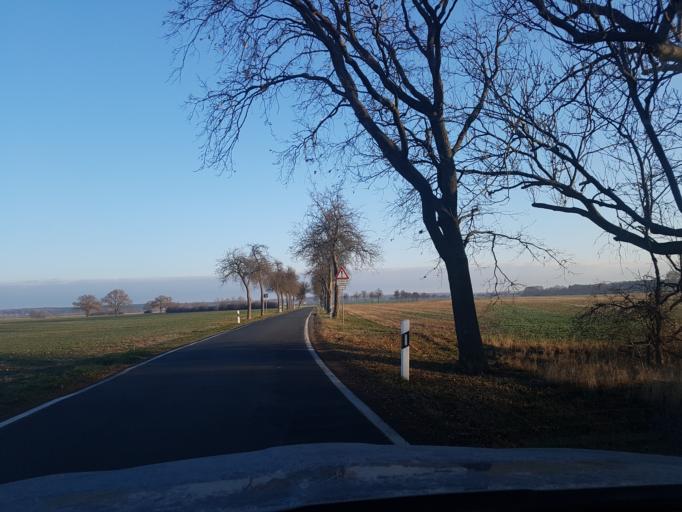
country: DE
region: Brandenburg
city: Schlieben
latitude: 51.7107
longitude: 13.3514
